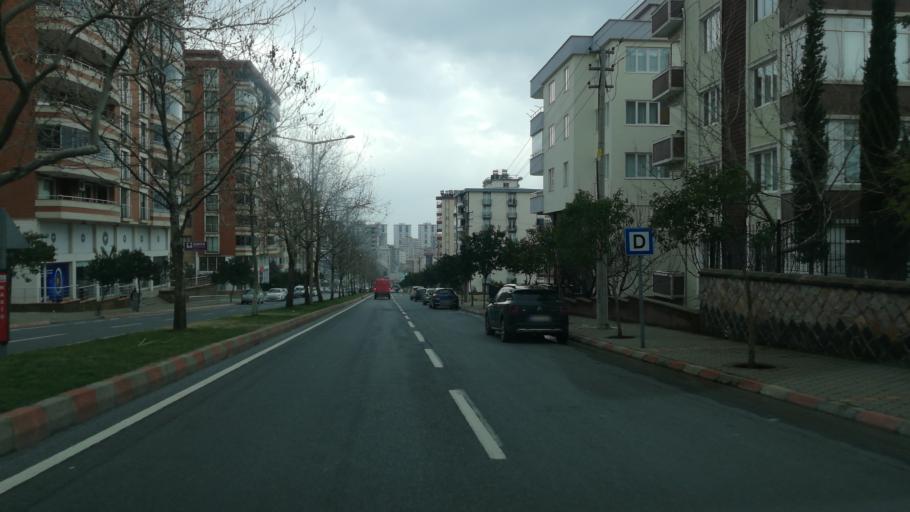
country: TR
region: Kahramanmaras
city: Kahramanmaras
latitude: 37.5860
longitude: 36.8788
